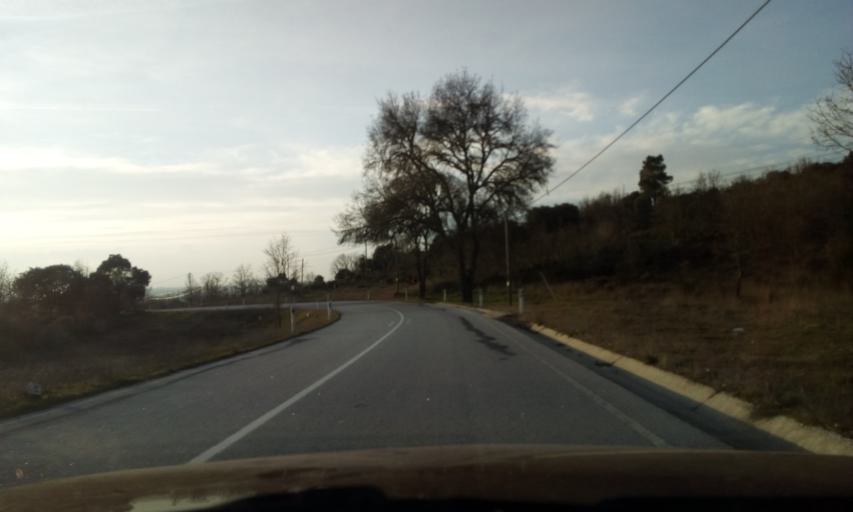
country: PT
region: Guarda
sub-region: Pinhel
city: Pinhel
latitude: 40.6026
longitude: -7.0130
